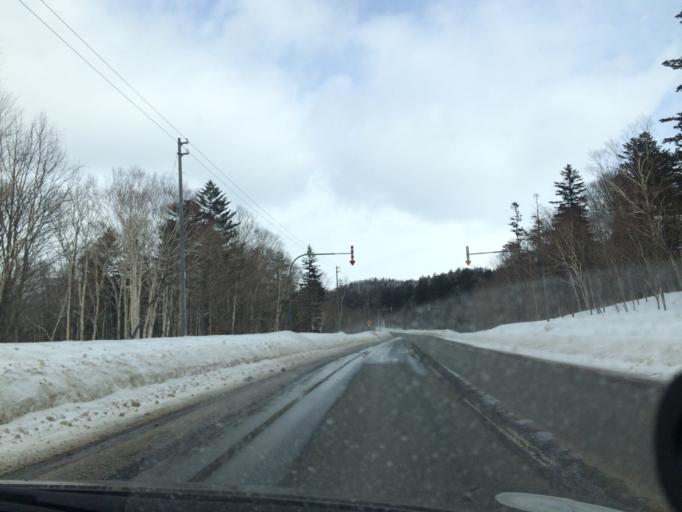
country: JP
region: Hokkaido
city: Shimo-furano
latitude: 43.1352
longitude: 142.7383
